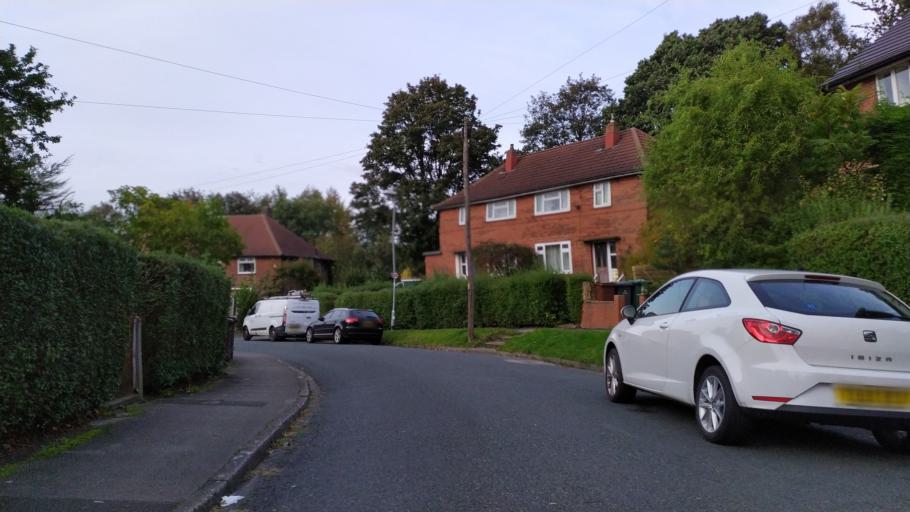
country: GB
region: England
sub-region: City and Borough of Leeds
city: Leeds
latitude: 53.8218
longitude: -1.5905
